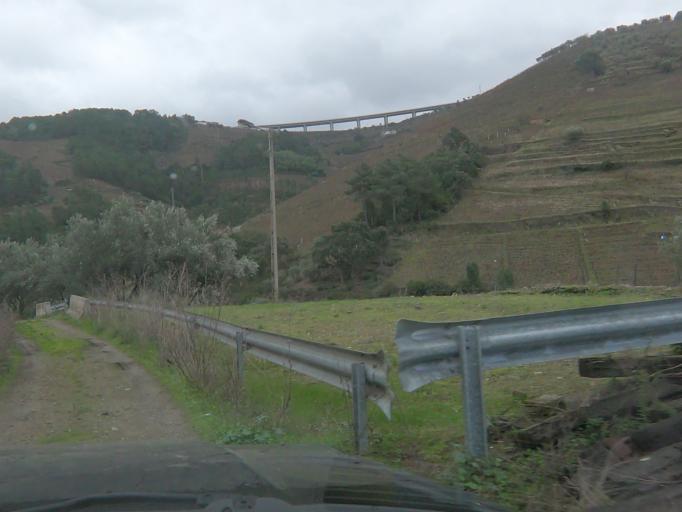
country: PT
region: Vila Real
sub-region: Vila Real
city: Vila Real
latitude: 41.2391
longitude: -7.7384
